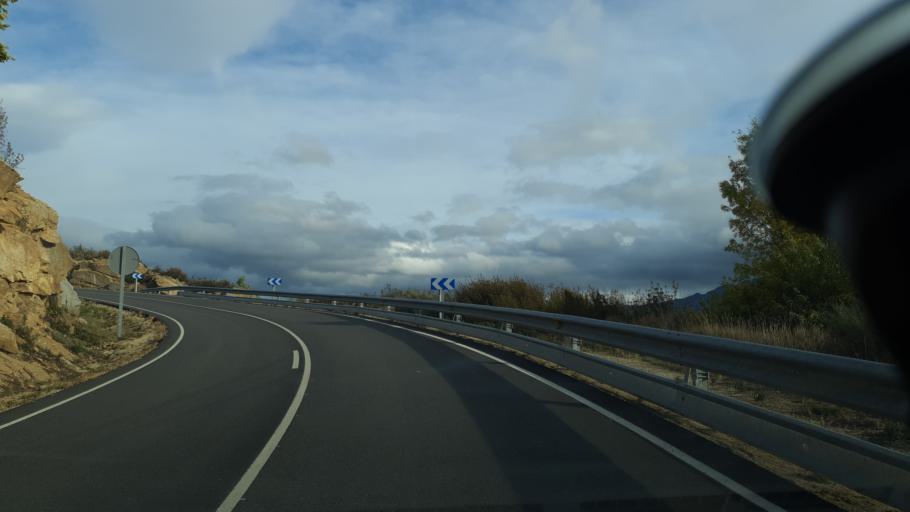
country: ES
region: Castille and Leon
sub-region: Provincia de Avila
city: Navalosa
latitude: 40.3982
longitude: -4.9081
